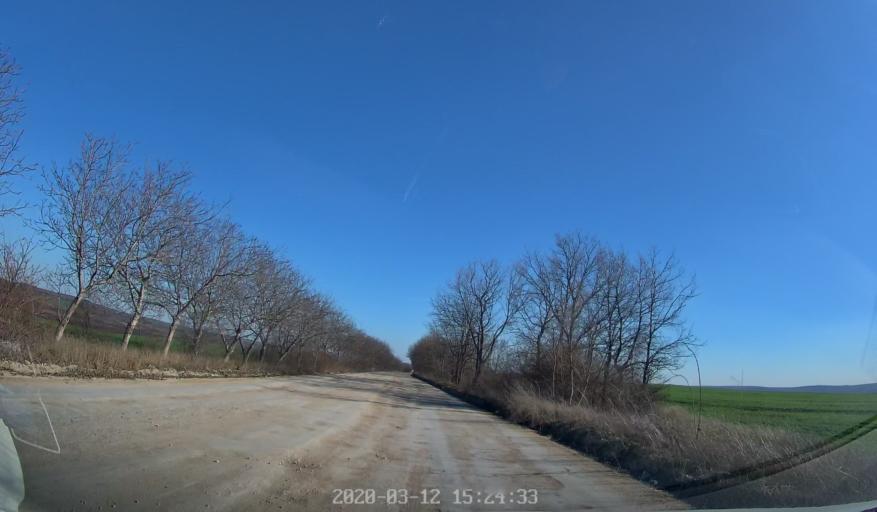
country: MD
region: Chisinau
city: Ciorescu
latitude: 47.1861
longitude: 28.9138
